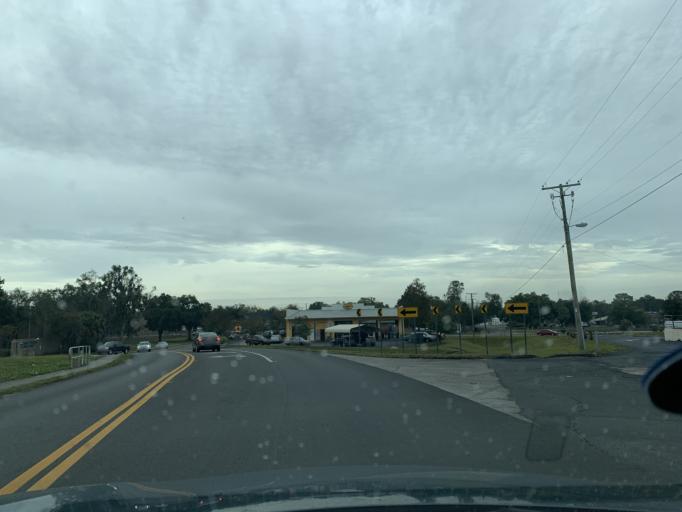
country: US
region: Florida
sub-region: Pasco County
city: Zephyrhills
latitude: 28.2457
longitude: -82.1880
